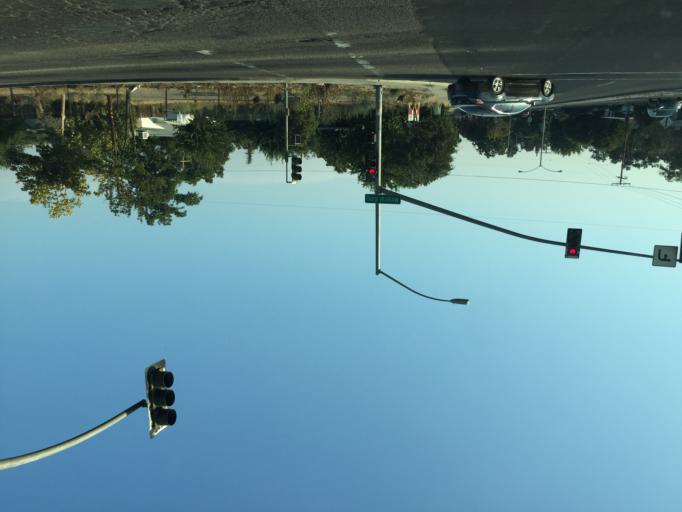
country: US
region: California
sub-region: Tulare County
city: Visalia
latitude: 36.3281
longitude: -119.2607
